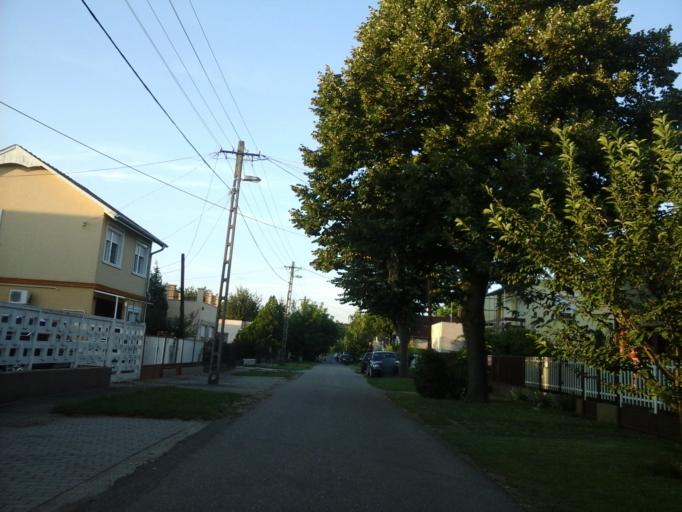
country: HU
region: Hajdu-Bihar
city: Hajduszoboszlo
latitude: 47.4590
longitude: 21.4048
